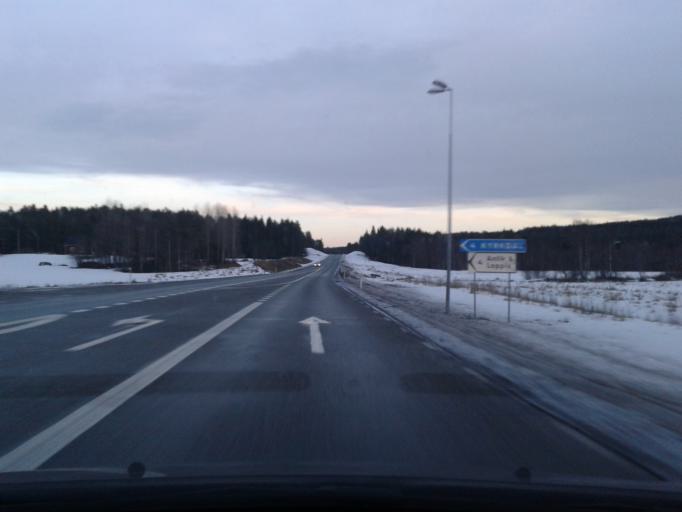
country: SE
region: Vaesternorrland
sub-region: Kramfors Kommun
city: Bollstabruk
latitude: 63.0749
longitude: 17.5570
